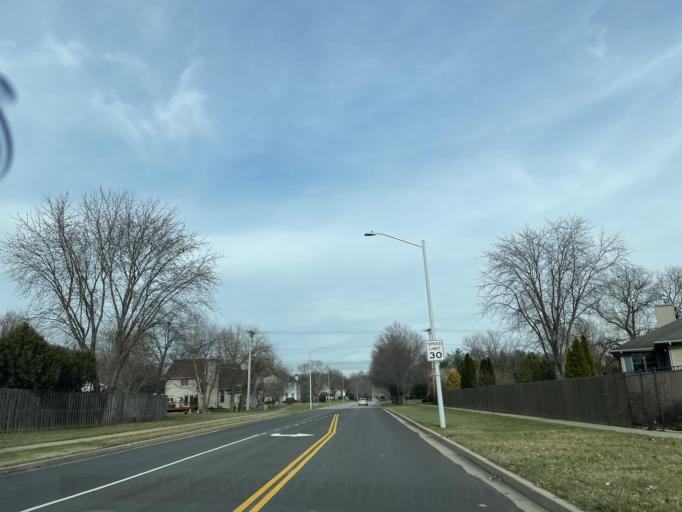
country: US
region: Illinois
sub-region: Sangamon County
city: Jerome
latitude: 39.7775
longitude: -89.7299
